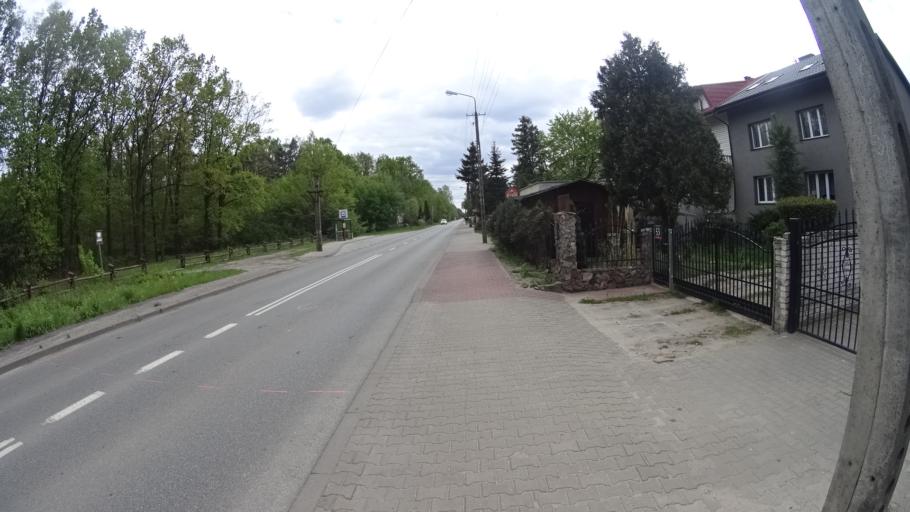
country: PL
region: Masovian Voivodeship
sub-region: Powiat warszawski zachodni
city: Babice
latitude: 52.2584
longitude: 20.8517
